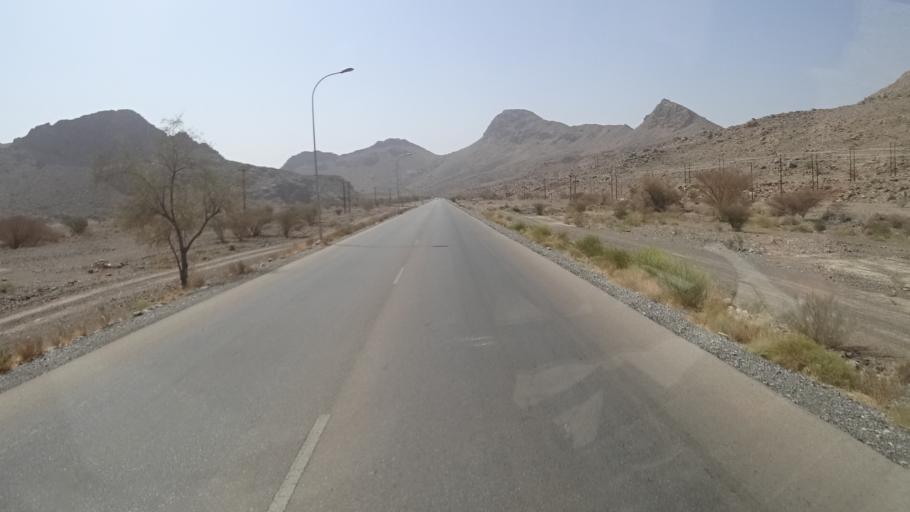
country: OM
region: Muhafazat ad Dakhiliyah
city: Bahla'
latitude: 23.0439
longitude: 57.3133
